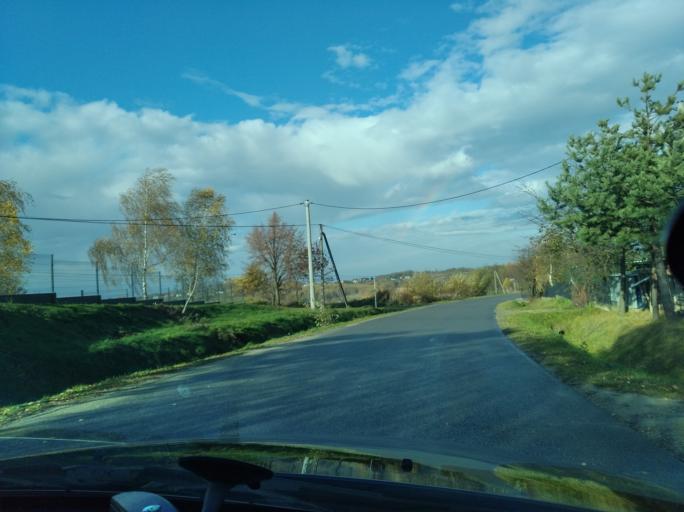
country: PL
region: Subcarpathian Voivodeship
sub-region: Powiat ropczycko-sedziszowski
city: Niedzwiada
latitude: 50.0146
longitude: 21.4780
